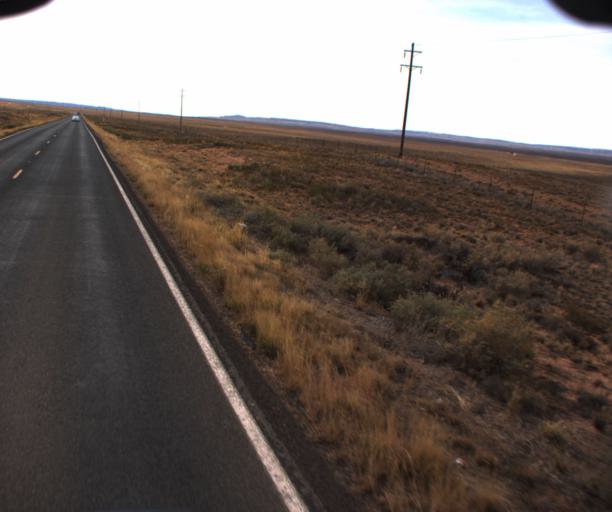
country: US
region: Arizona
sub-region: Apache County
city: Ganado
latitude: 35.9098
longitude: -109.6117
